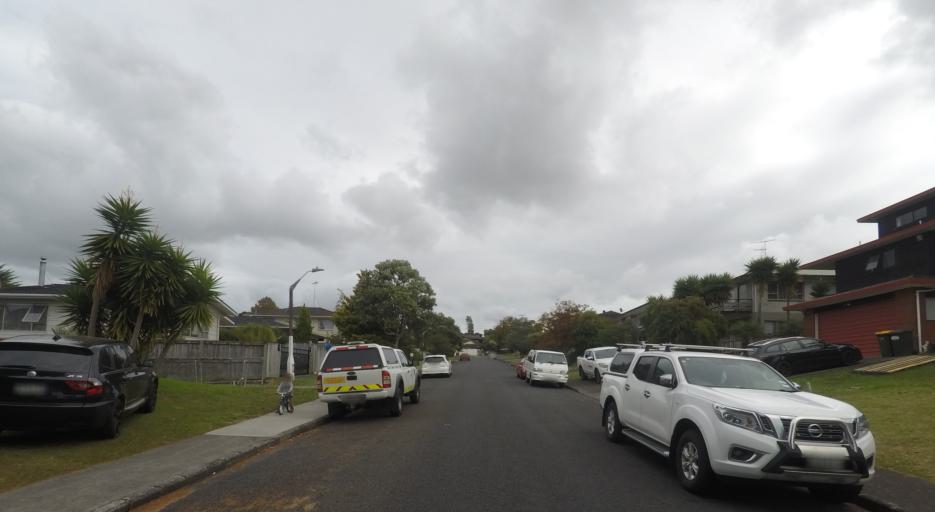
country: NZ
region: Auckland
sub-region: Auckland
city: Rosebank
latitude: -36.8825
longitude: 174.6493
